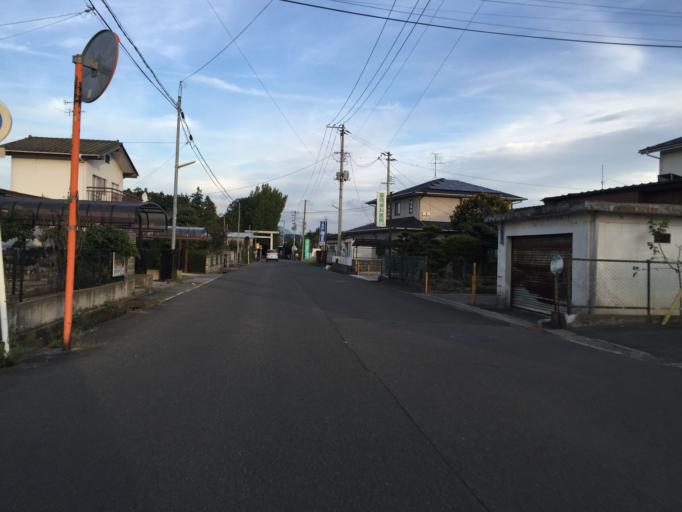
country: JP
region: Fukushima
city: Fukushima-shi
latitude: 37.8018
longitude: 140.4926
